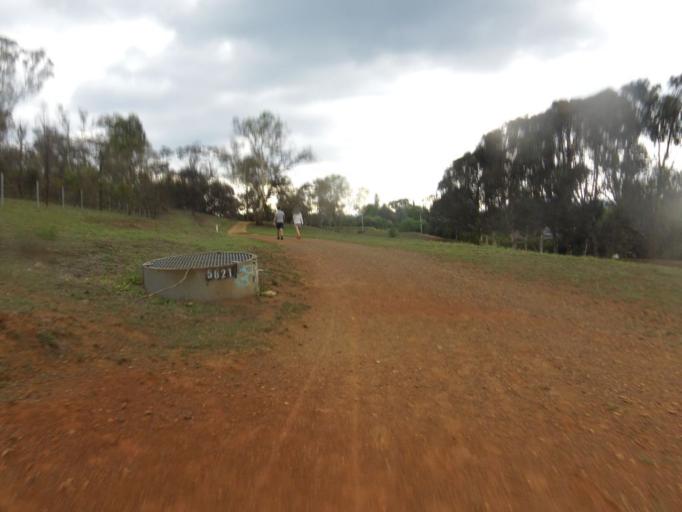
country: AU
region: Australian Capital Territory
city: Forrest
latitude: -35.3292
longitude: 149.1207
